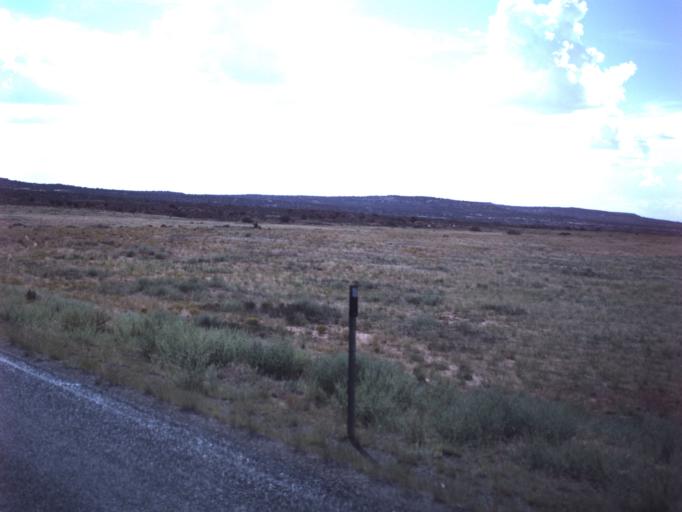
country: US
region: Utah
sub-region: Grand County
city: Moab
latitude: 38.6181
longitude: -109.8134
